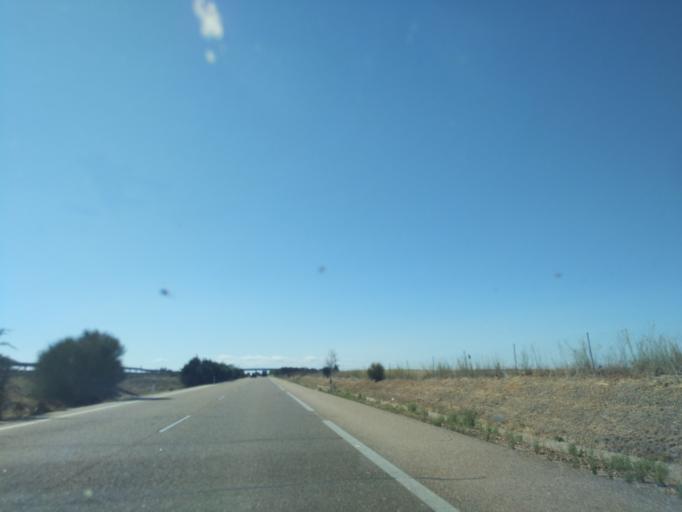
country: ES
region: Castille and Leon
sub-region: Provincia de Zamora
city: Cerecinos de Campos
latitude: 41.9183
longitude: -5.5154
